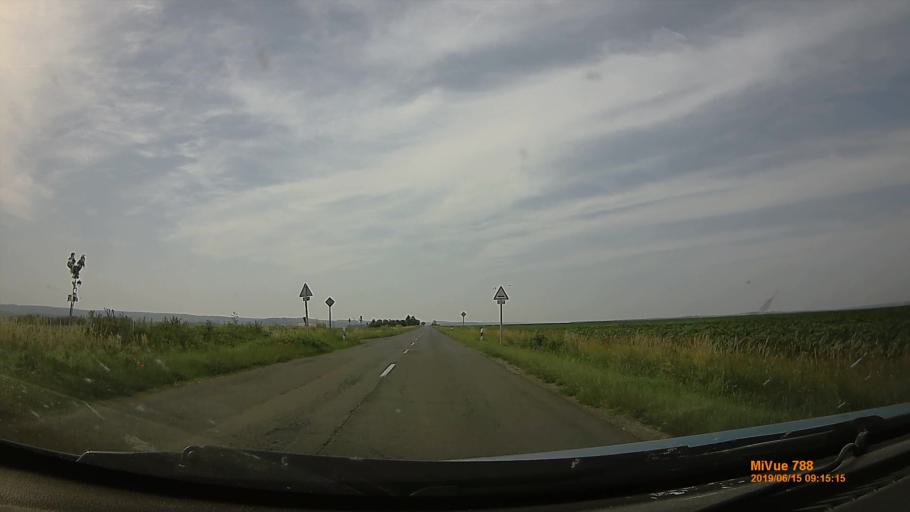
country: HU
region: Tolna
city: Iregszemcse
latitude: 46.6322
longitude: 18.1999
